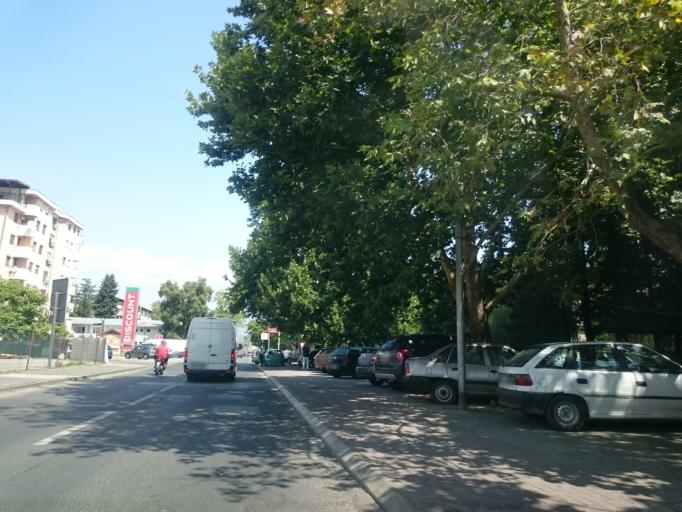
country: MK
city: Krushopek
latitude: 42.0056
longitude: 21.3830
